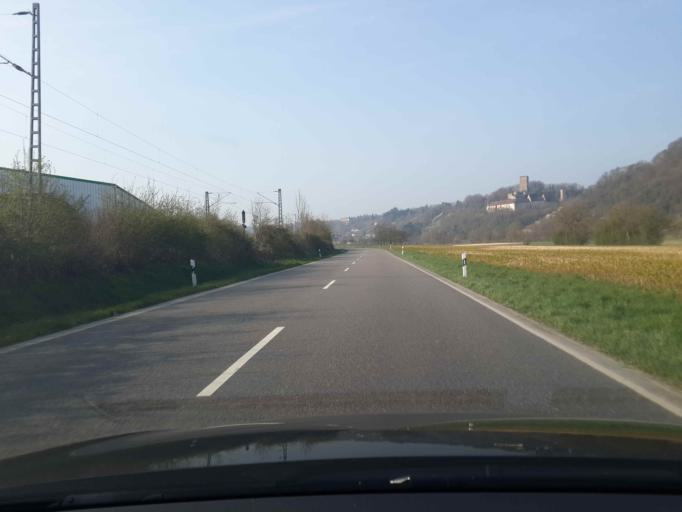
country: DE
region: Baden-Wuerttemberg
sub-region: Regierungsbezirk Stuttgart
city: Gundelsheim
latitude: 49.2745
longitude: 9.1549
